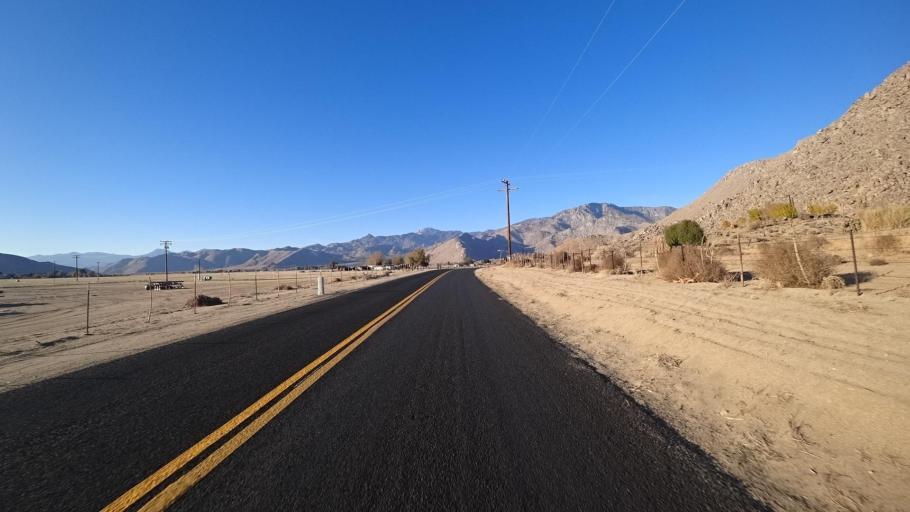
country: US
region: California
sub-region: Kern County
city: Weldon
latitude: 35.6522
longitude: -118.2533
